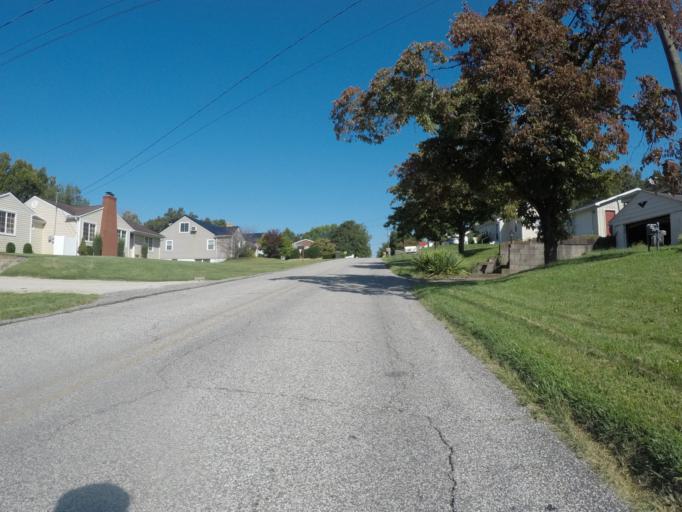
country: US
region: Kentucky
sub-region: Boyd County
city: Westwood
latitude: 38.4857
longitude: -82.6874
